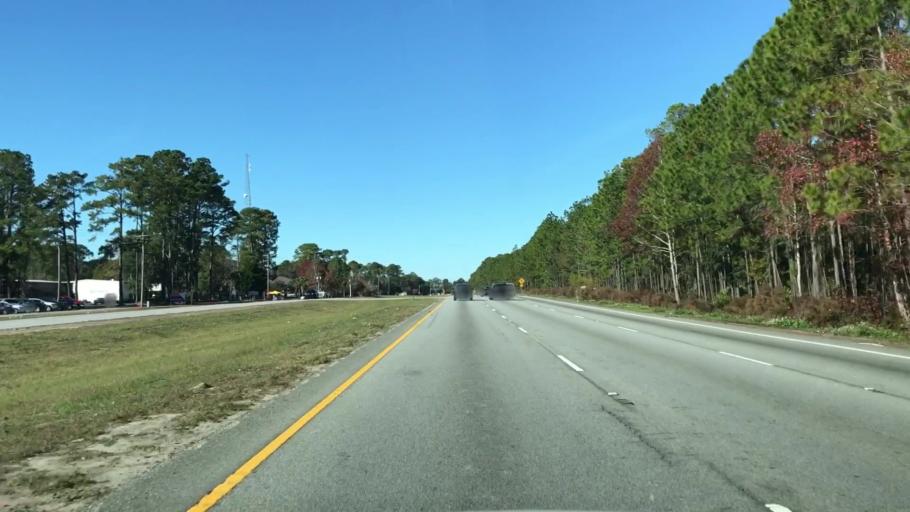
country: US
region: South Carolina
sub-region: Beaufort County
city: Bluffton
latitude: 32.2488
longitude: -80.8350
